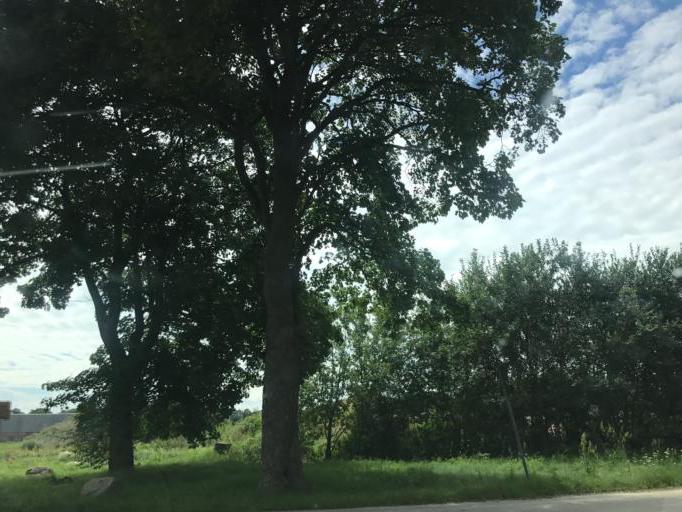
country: DE
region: Mecklenburg-Vorpommern
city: Rechlin
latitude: 53.3262
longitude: 12.7603
